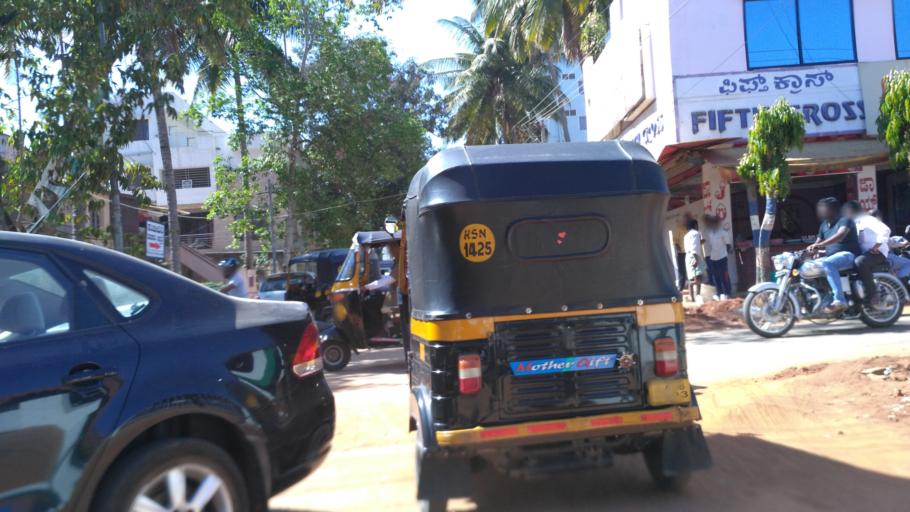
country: IN
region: Karnataka
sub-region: Hassan
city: Hassan
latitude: 13.0068
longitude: 76.1074
